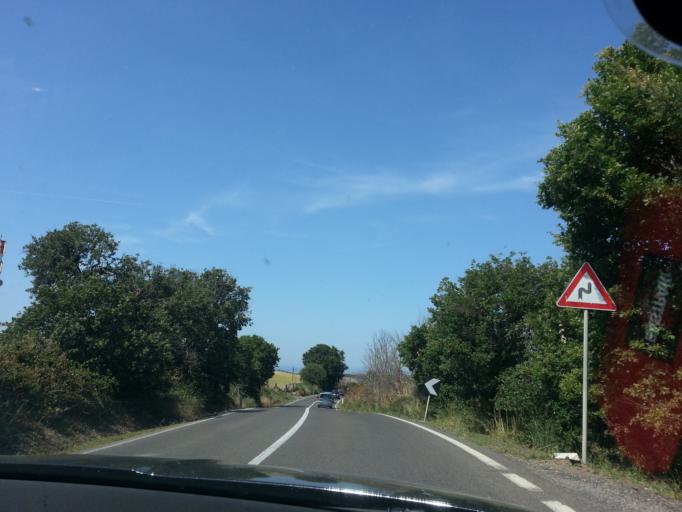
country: IT
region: Latium
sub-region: Provincia di Viterbo
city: Tarquinia
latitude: 42.2603
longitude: 11.8262
